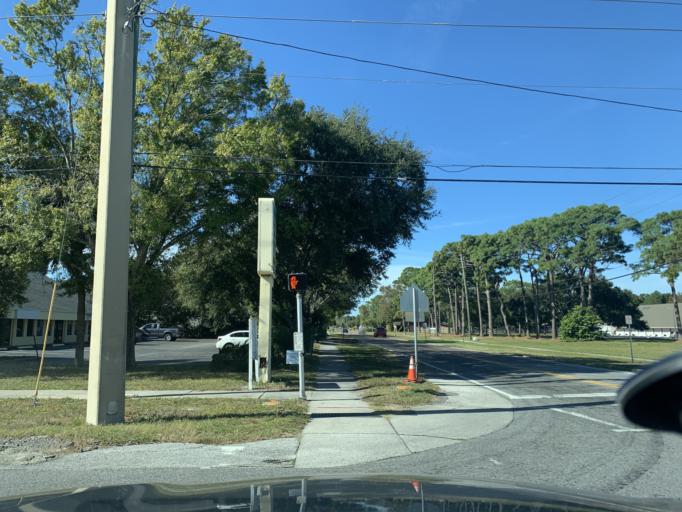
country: US
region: Florida
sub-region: Pinellas County
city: Seminole
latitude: 27.8503
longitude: -82.7623
